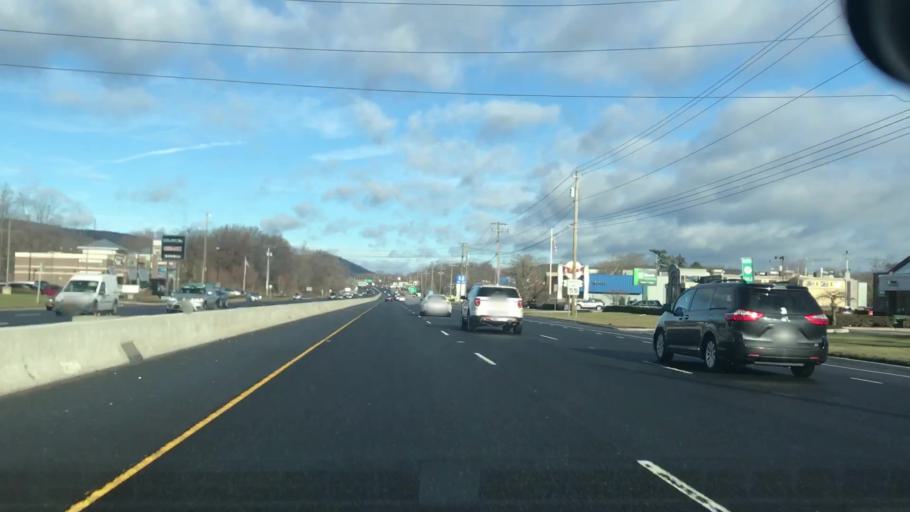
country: US
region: New Jersey
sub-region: Bergen County
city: Mahwah
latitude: 41.0834
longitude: -74.1511
